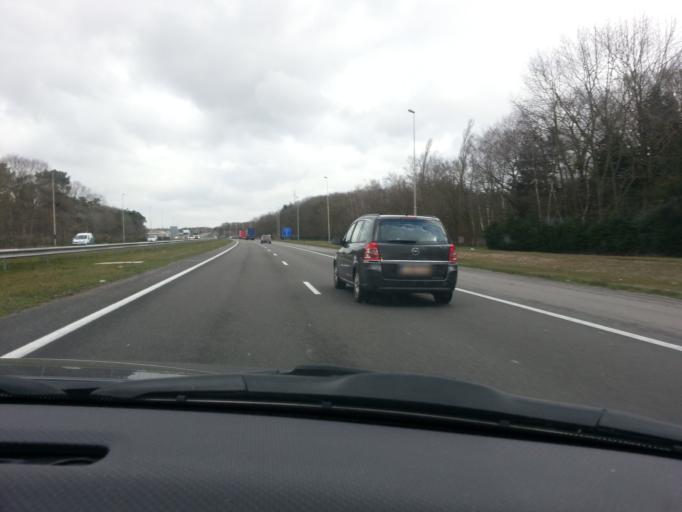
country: NL
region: North Brabant
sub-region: Gemeente Loon op Zand
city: Loon op Zand
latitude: 51.6123
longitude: 5.0710
